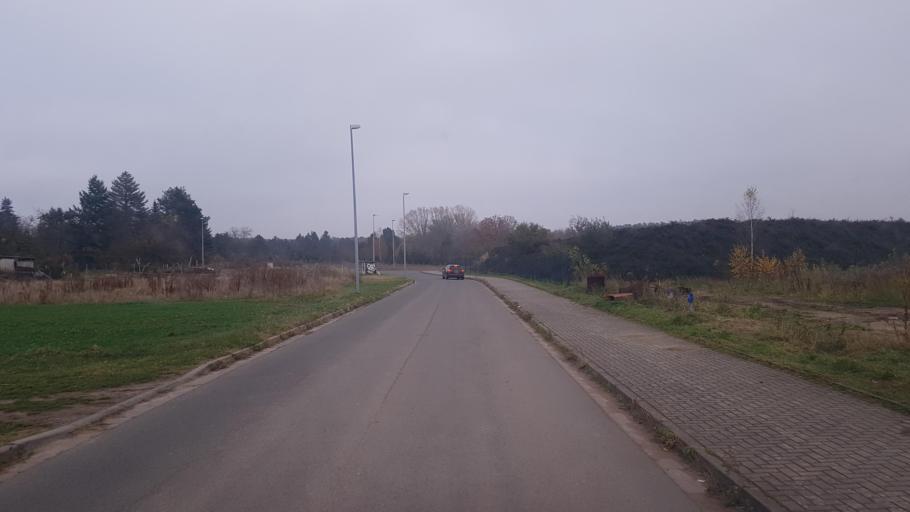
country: DE
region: Brandenburg
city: Gross Kreutz
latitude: 52.4062
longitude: 12.7321
